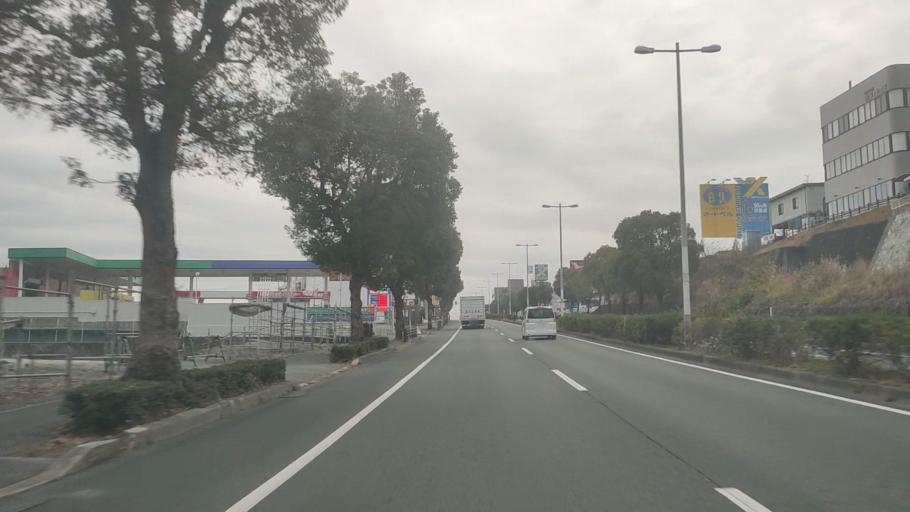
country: JP
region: Kumamoto
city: Kumamoto
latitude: 32.8205
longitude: 130.7576
